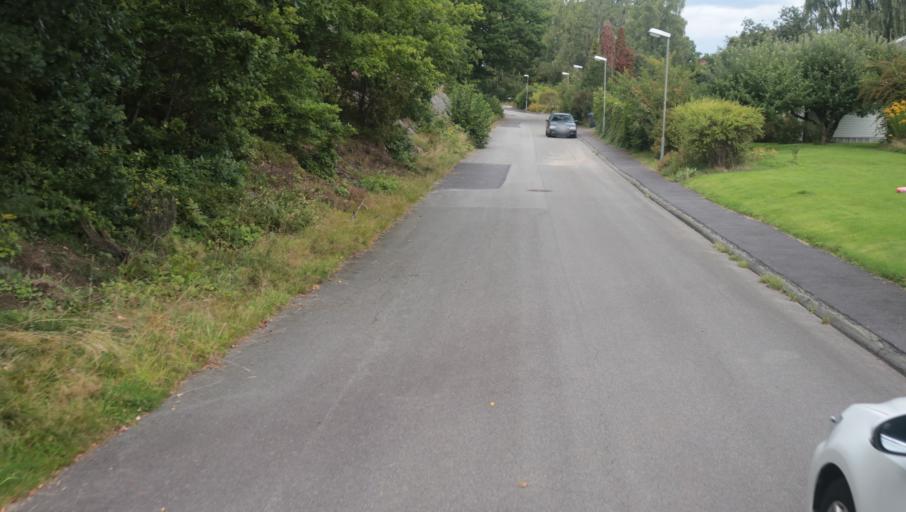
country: SE
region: Blekinge
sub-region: Karlshamns Kommun
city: Karlshamn
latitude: 56.1728
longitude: 14.8517
